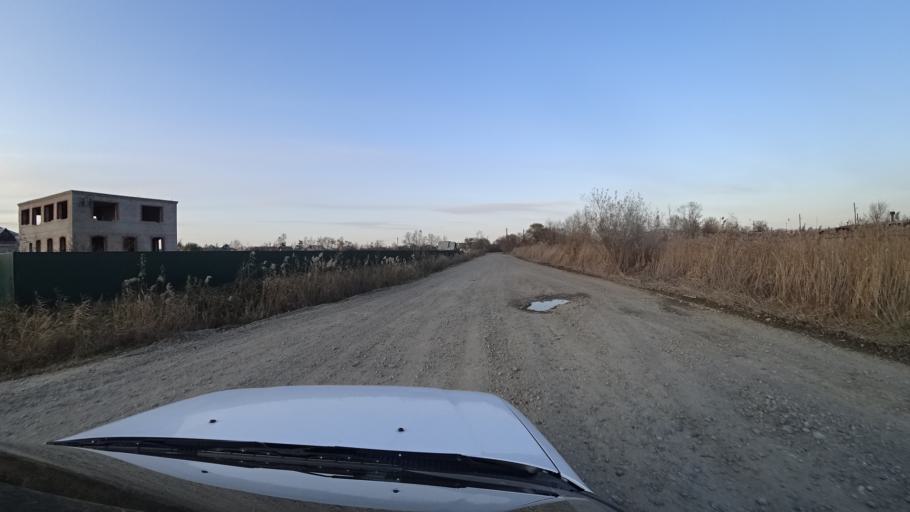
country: RU
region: Primorskiy
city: Dal'nerechensk
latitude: 45.9387
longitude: 133.8206
